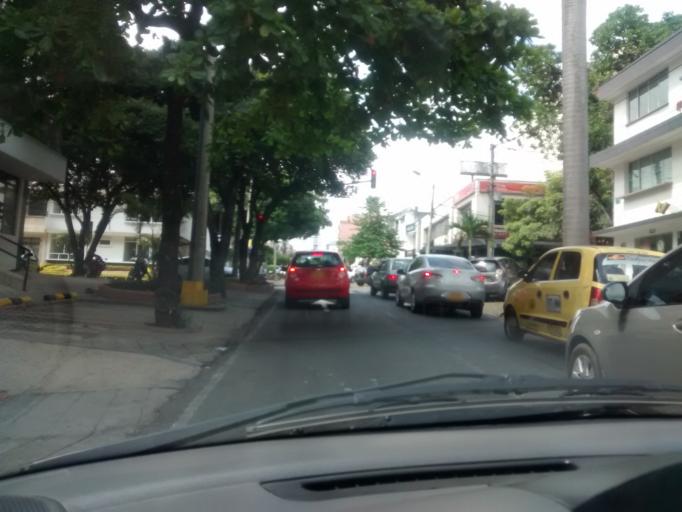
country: CO
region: Santander
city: Bucaramanga
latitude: 7.1212
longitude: -73.1095
